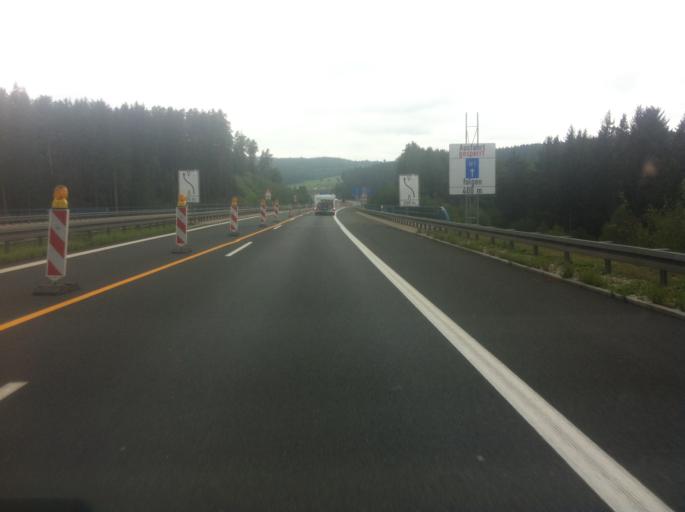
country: DE
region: Bavaria
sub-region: Upper Palatinate
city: Wernberg-Koblitz
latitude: 49.5249
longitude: 12.1778
